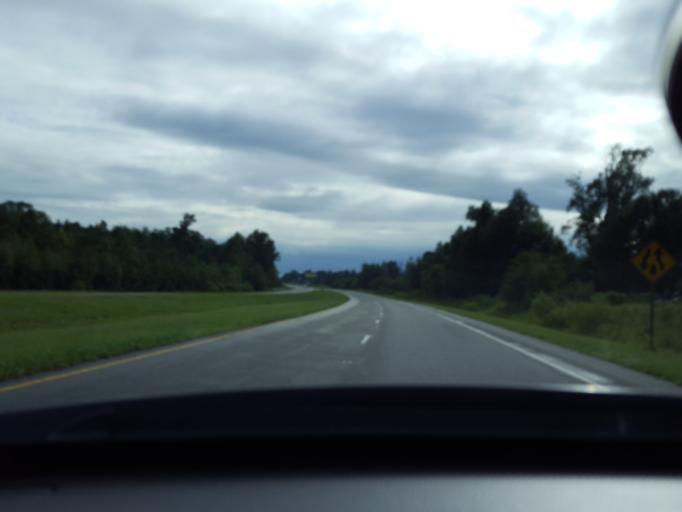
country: US
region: North Carolina
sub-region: Duplin County
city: Kenansville
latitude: 34.9269
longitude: -78.0128
